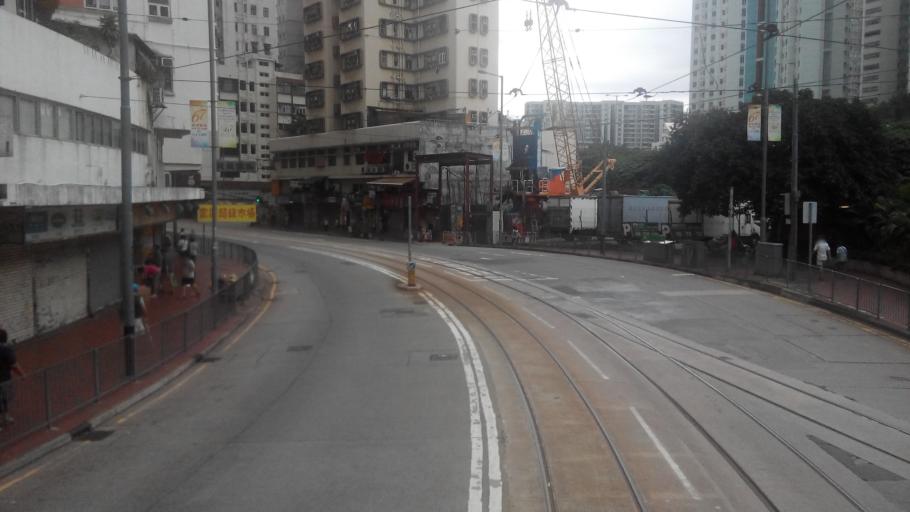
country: HK
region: Wanchai
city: Wan Chai
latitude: 22.2800
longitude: 114.2254
